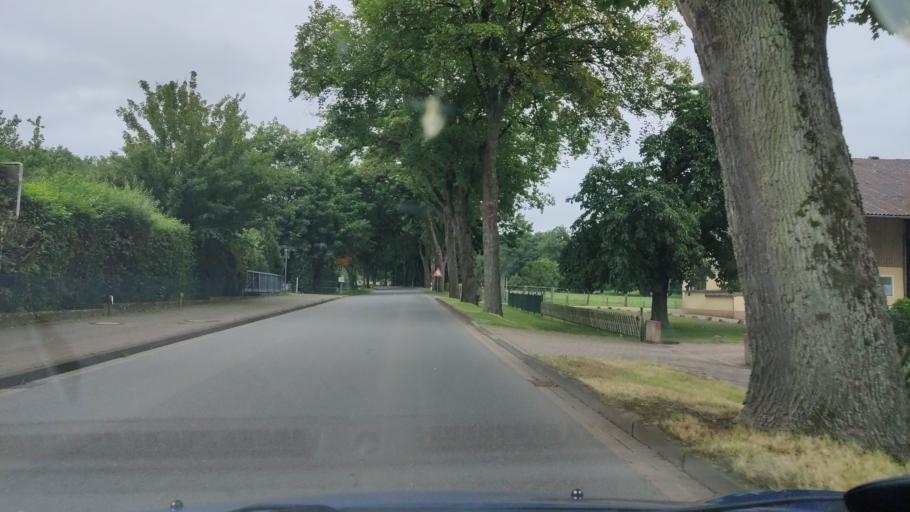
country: DE
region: Lower Saxony
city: Holzminden
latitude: 51.8207
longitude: 9.4712
